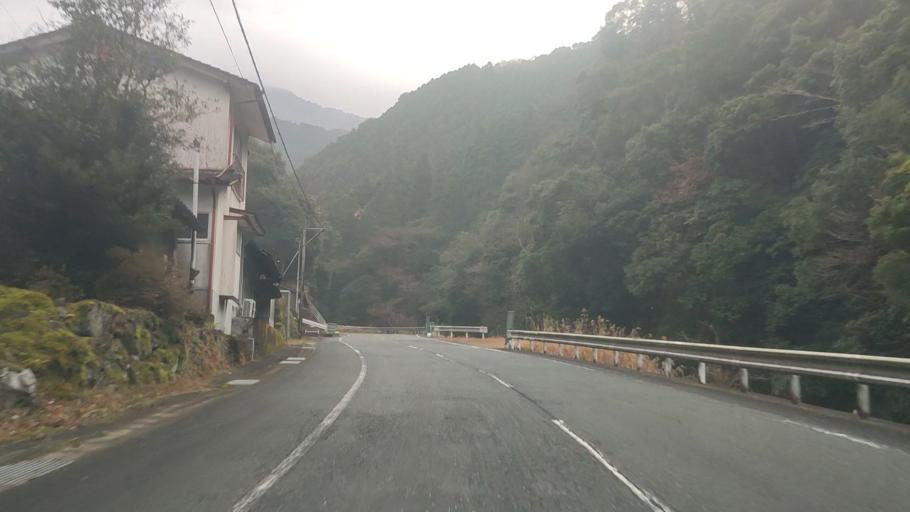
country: JP
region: Kumamoto
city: Matsubase
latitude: 32.6023
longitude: 130.8870
